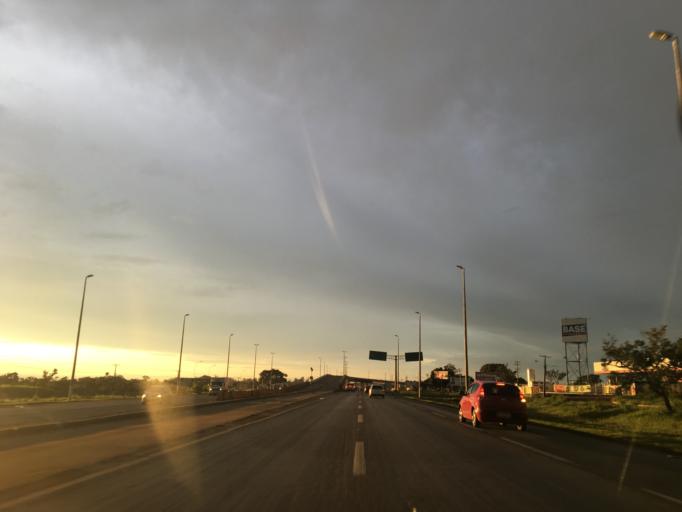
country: BR
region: Federal District
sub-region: Brasilia
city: Brasilia
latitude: -15.9965
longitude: -47.9855
